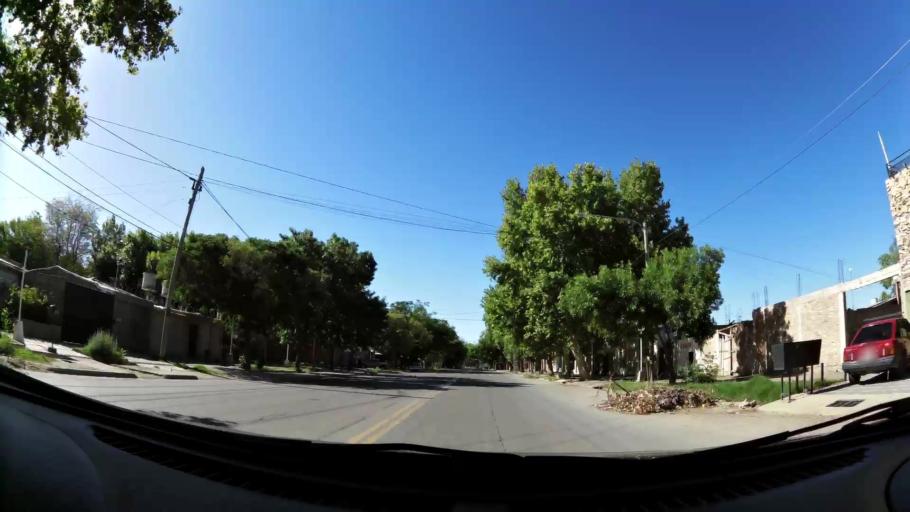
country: AR
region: Mendoza
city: Las Heras
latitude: -32.8458
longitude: -68.8202
